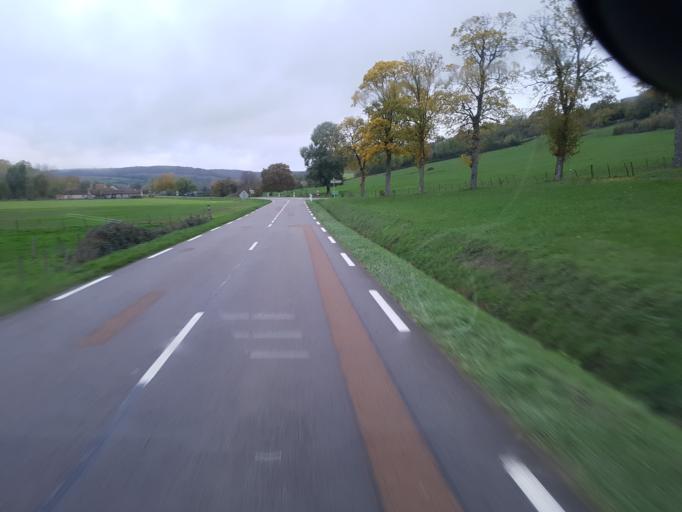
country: FR
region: Bourgogne
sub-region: Departement de la Cote-d'Or
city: Chatillon-sur-Seine
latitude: 47.6967
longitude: 4.6403
